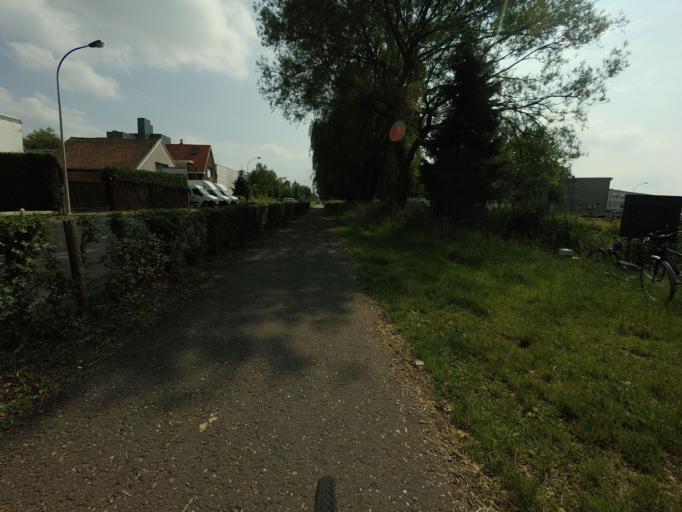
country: BE
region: Flanders
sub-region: Provincie Antwerpen
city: Schoten
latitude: 51.2496
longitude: 4.5062
